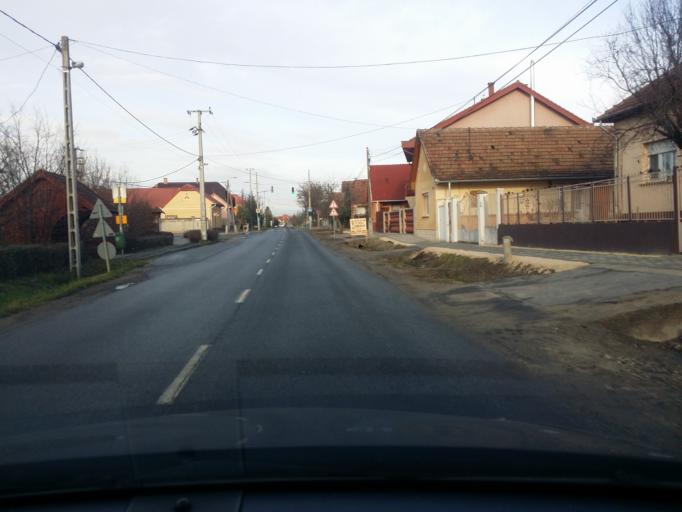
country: HU
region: Pest
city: Alsonemedi
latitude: 47.3184
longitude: 19.1548
